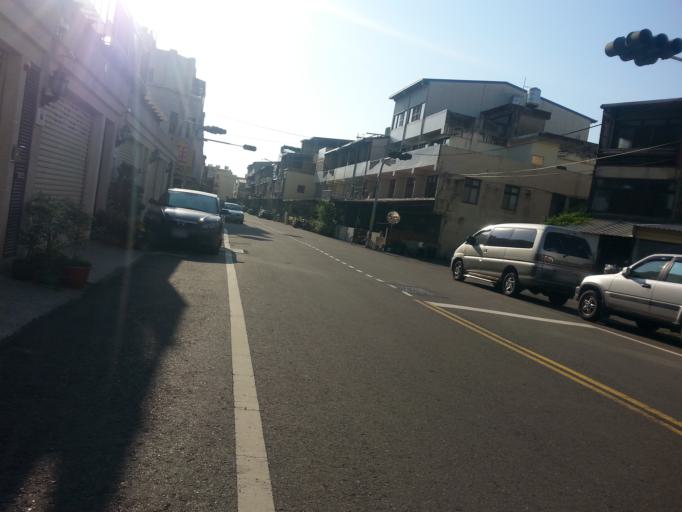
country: TW
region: Taiwan
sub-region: Changhua
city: Chang-hua
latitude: 24.0900
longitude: 120.5476
